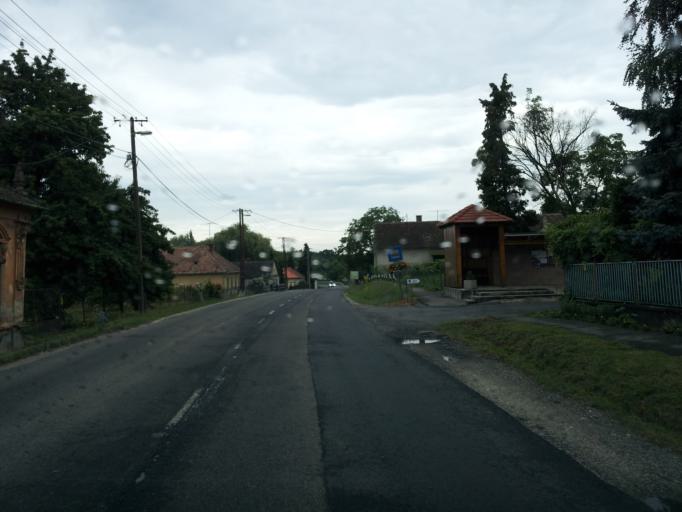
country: HU
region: Vas
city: Kormend
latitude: 46.9601
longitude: 16.6414
